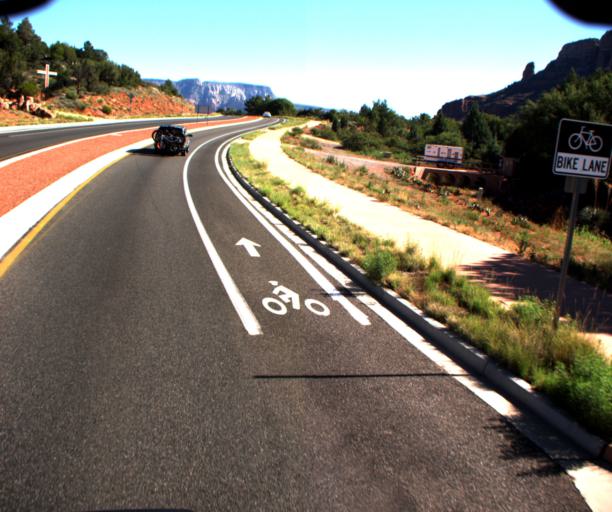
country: US
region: Arizona
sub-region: Coconino County
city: Sedona
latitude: 34.8267
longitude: -111.7786
